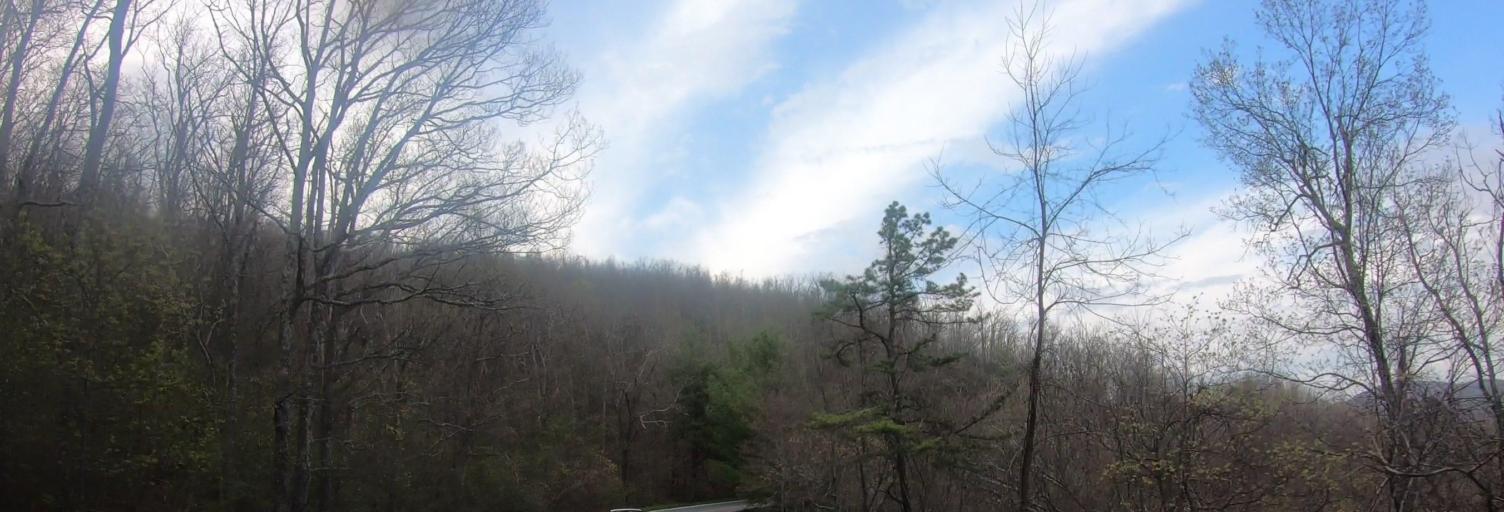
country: US
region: Virginia
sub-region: Augusta County
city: Crimora
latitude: 38.1807
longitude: -78.7595
